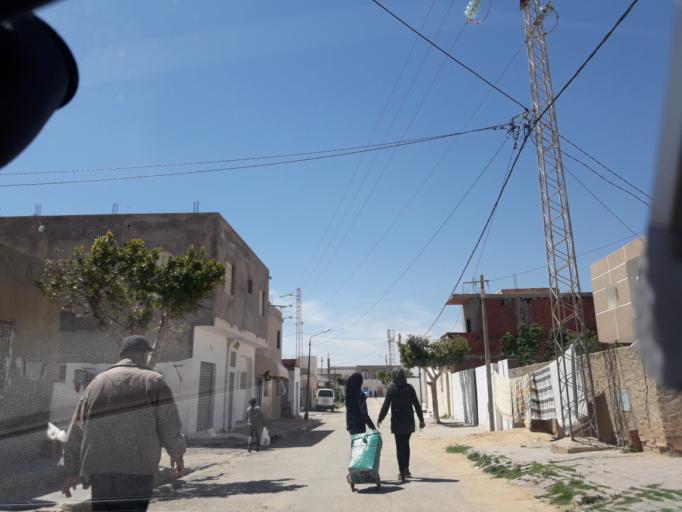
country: TN
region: Safaqis
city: Sfax
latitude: 34.7404
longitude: 10.5227
